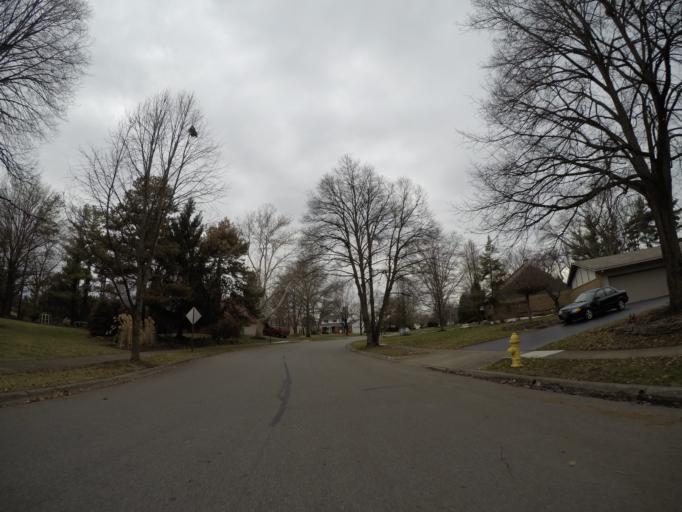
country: US
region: Ohio
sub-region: Franklin County
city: Upper Arlington
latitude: 40.0498
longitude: -83.0711
